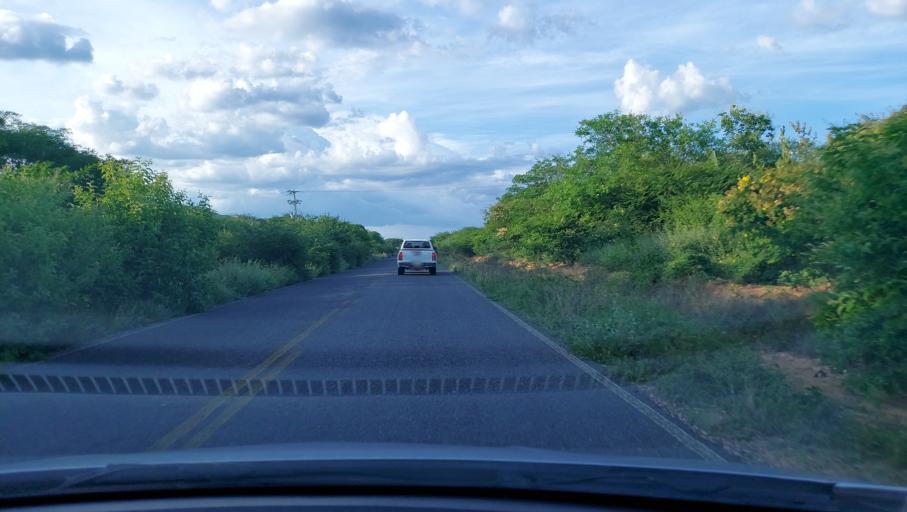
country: BR
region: Bahia
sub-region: Oliveira Dos Brejinhos
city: Beira Rio
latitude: -12.1897
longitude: -42.5384
